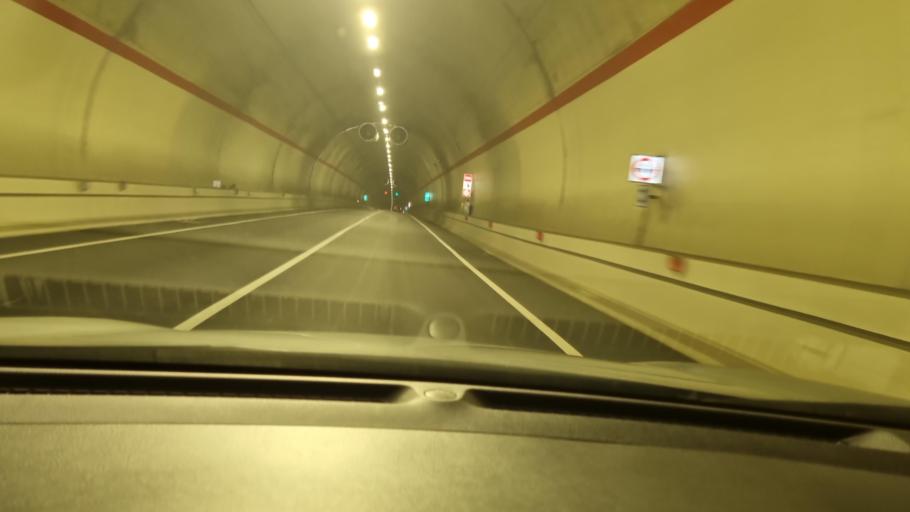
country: IT
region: Lombardy
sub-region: Provincia di Bergamo
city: Zogno
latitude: 45.8057
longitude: 9.6708
